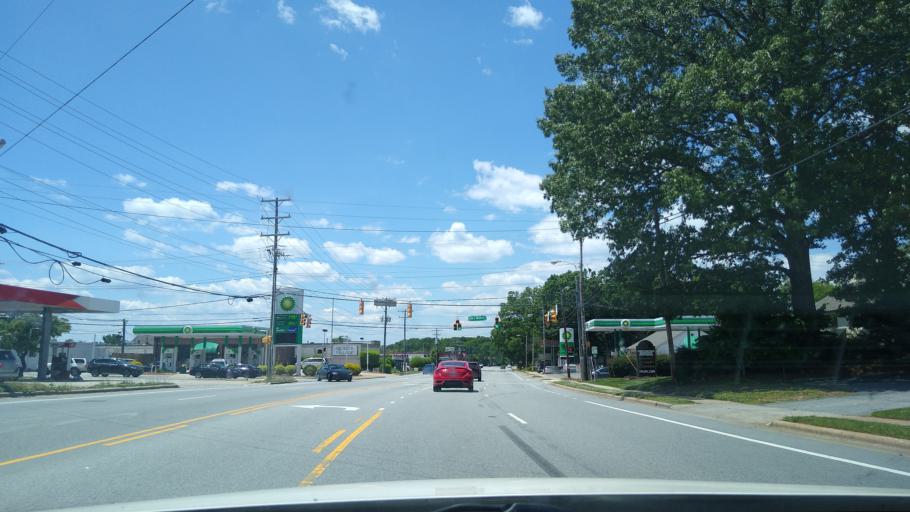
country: US
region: North Carolina
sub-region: Guilford County
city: Greensboro
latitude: 36.0892
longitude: -79.8837
